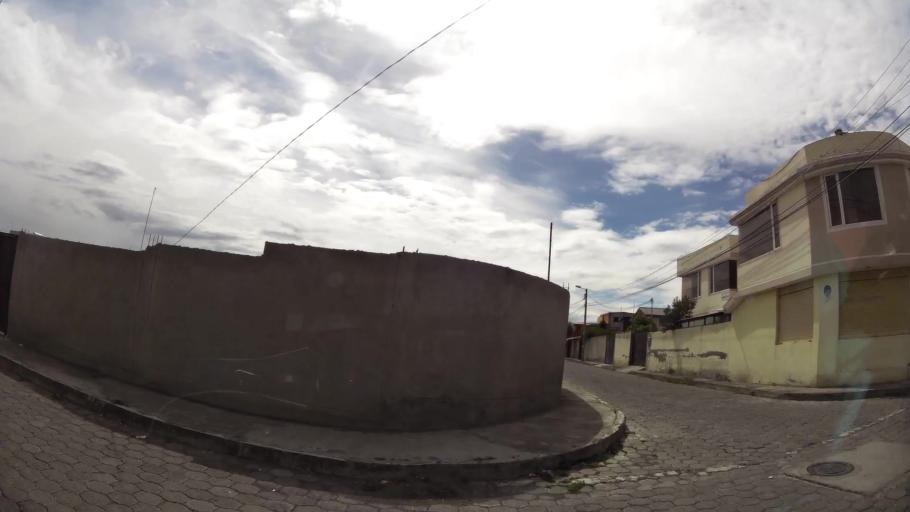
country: EC
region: Cotopaxi
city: Latacunga
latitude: -0.9294
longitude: -78.6004
